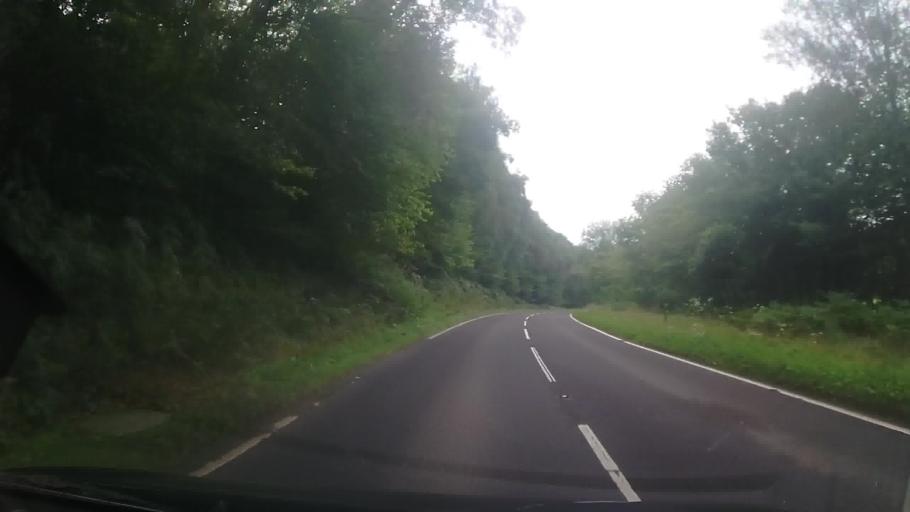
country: GB
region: Wales
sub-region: Gwynedd
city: Corris
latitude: 52.6168
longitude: -3.7643
